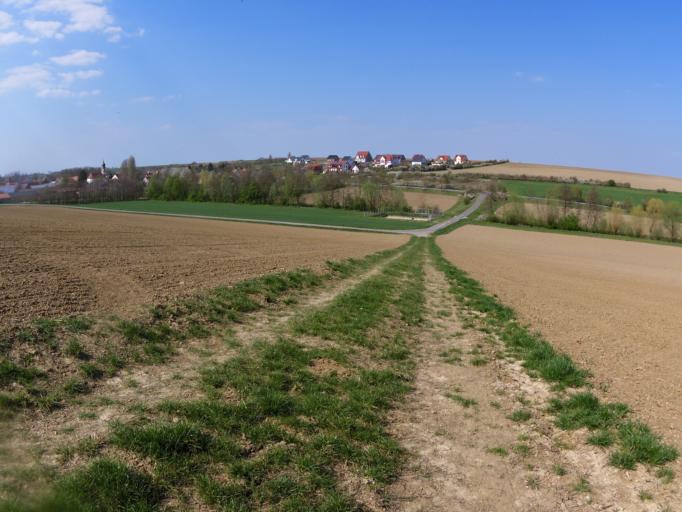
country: DE
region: Bavaria
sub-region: Regierungsbezirk Unterfranken
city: Dettelbach
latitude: 49.8200
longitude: 10.1317
